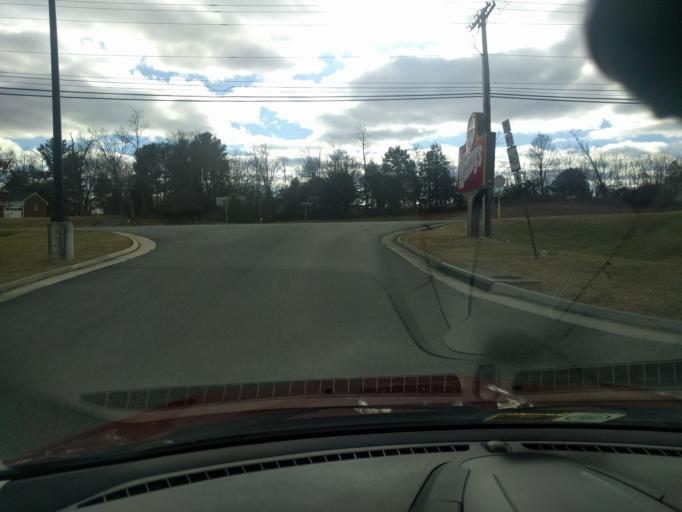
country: US
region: Virginia
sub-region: City of Bedford
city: Bedford
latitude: 37.3248
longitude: -79.4992
